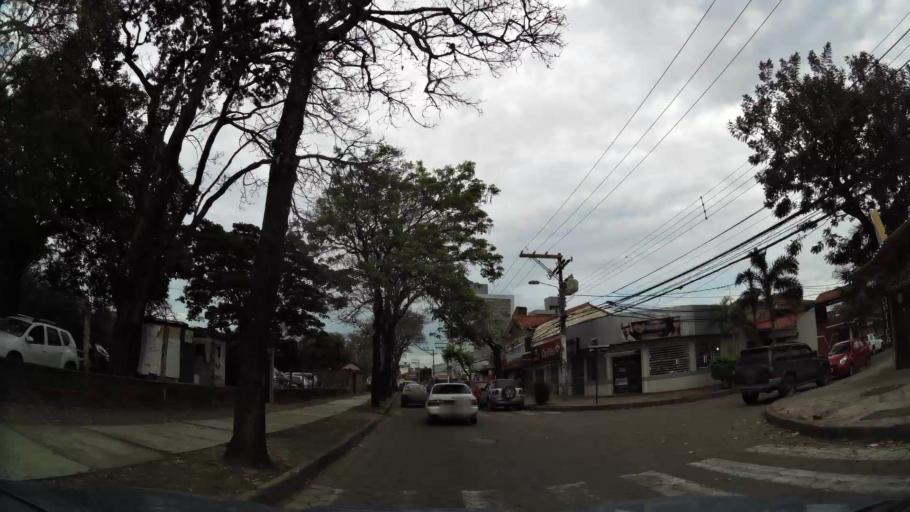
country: BO
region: Santa Cruz
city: Santa Cruz de la Sierra
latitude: -17.7731
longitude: -63.1706
